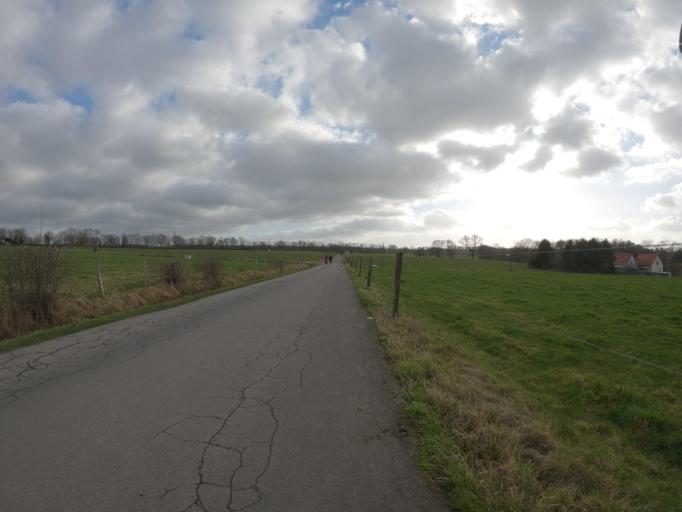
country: DE
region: North Rhine-Westphalia
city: Stolberg
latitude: 50.7736
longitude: 6.1710
